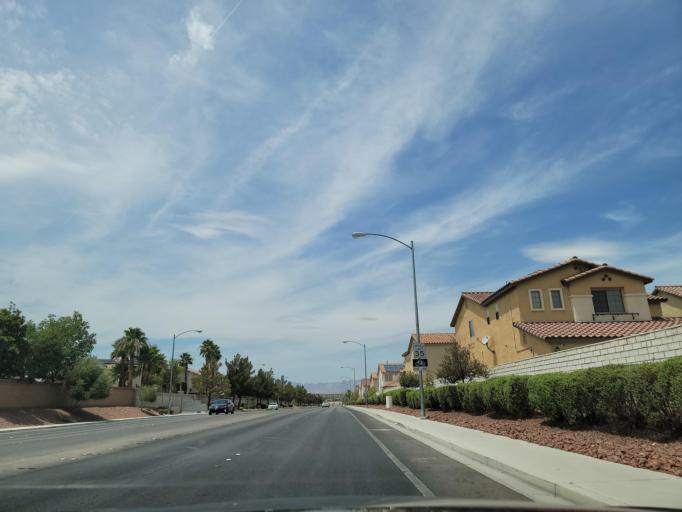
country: US
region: Nevada
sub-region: Clark County
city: Paradise
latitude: 36.0207
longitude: -115.1458
